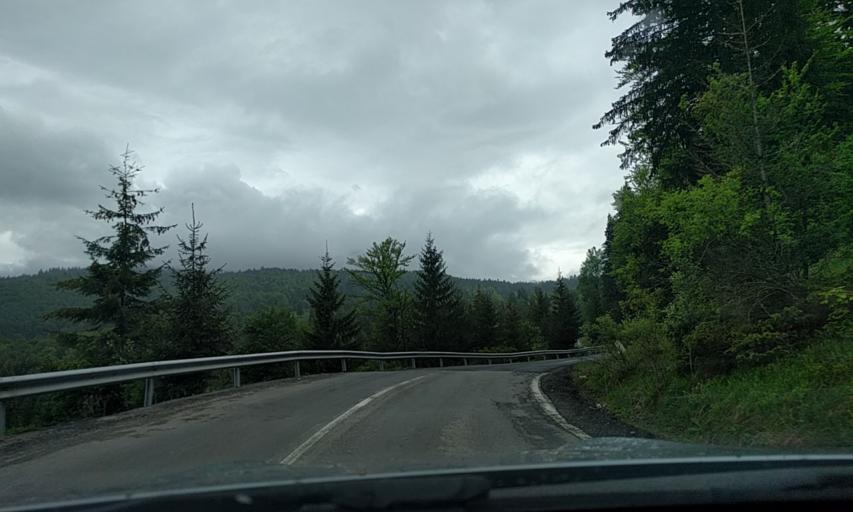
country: RO
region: Prahova
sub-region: Oras Sinaia
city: Sinaia
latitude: 45.3015
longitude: 25.5203
